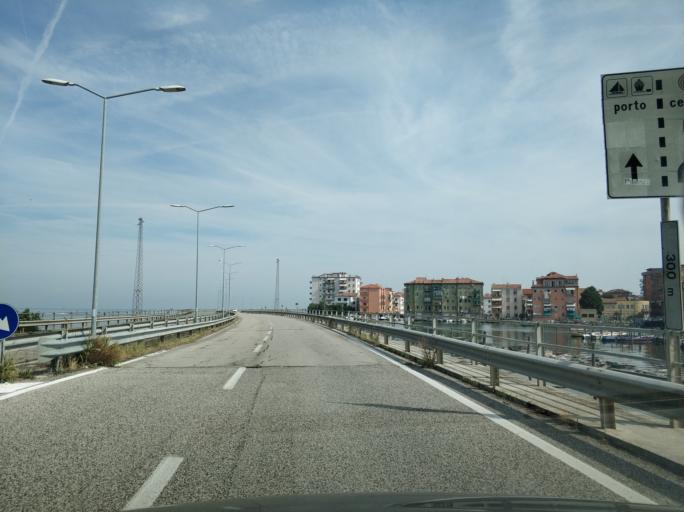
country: IT
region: Veneto
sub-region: Provincia di Venezia
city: Chioggia
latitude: 45.2129
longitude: 12.2731
